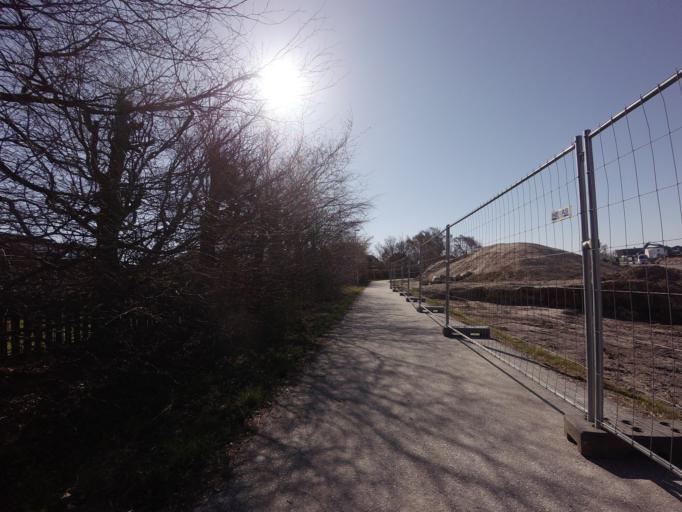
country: SE
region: Skane
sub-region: Malmo
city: Oxie
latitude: 55.4725
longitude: 13.1337
